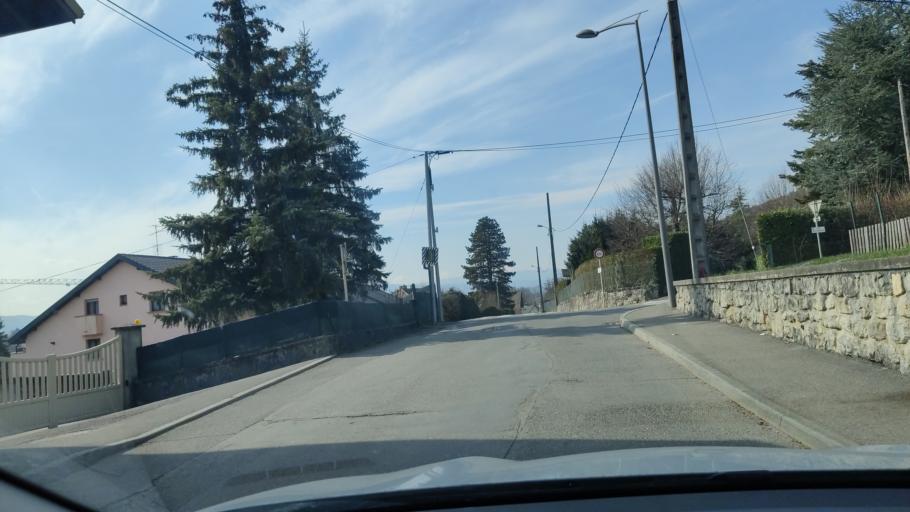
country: FR
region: Rhone-Alpes
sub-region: Departement de la Haute-Savoie
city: Bonneville
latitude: 46.0850
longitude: 6.4068
